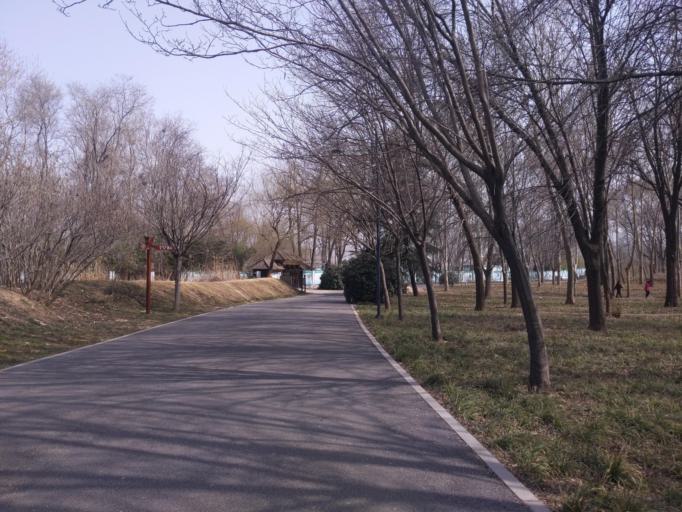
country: CN
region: Henan Sheng
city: Puyang
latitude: 35.7786
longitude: 114.9581
